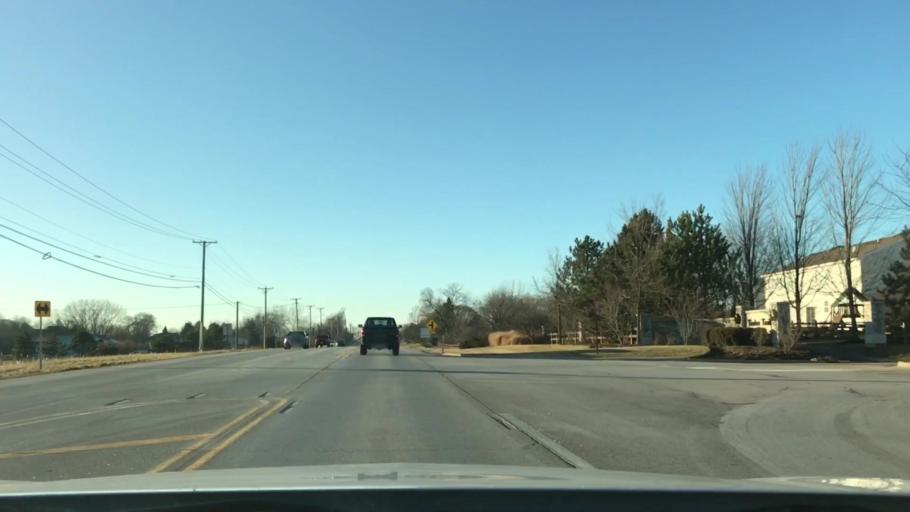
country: US
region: Illinois
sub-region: Kane County
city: Gilberts
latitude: 42.0778
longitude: -88.3728
